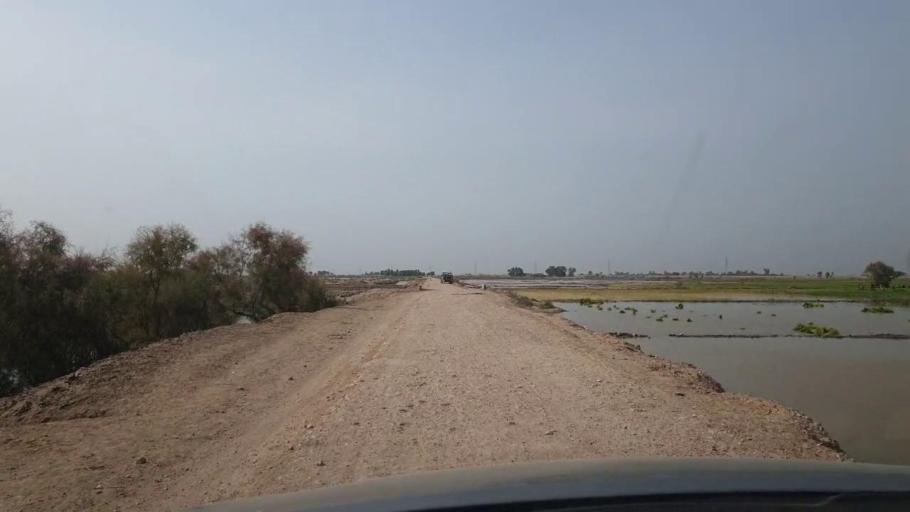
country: PK
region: Sindh
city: Lakhi
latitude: 27.8425
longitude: 68.6997
